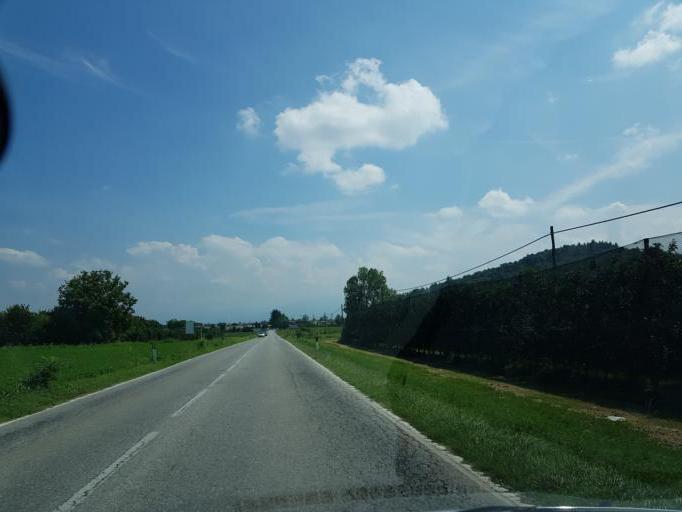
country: IT
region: Piedmont
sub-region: Provincia di Cuneo
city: Caraglio
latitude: 44.4365
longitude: 7.4171
